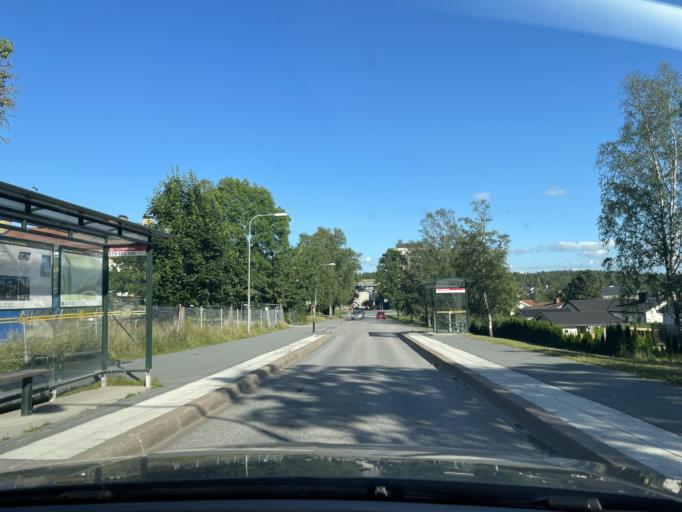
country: SE
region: Stockholm
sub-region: Sigtuna Kommun
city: Marsta
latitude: 59.6228
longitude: 17.8523
